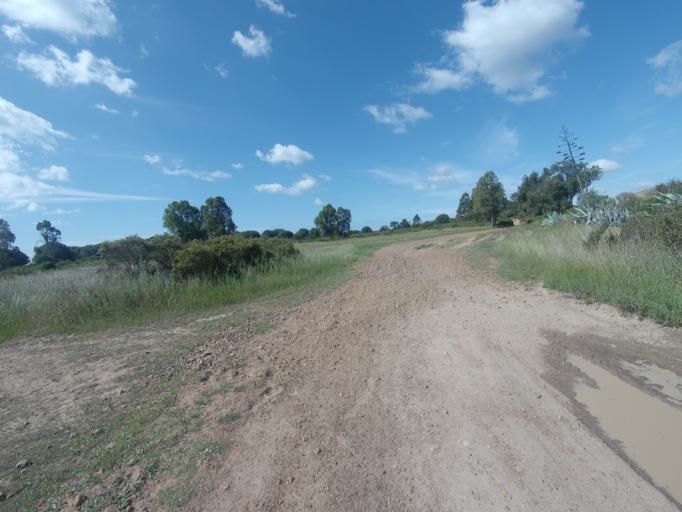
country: ES
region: Andalusia
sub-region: Provincia de Huelva
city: Aljaraque
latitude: 37.2359
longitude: -7.0309
